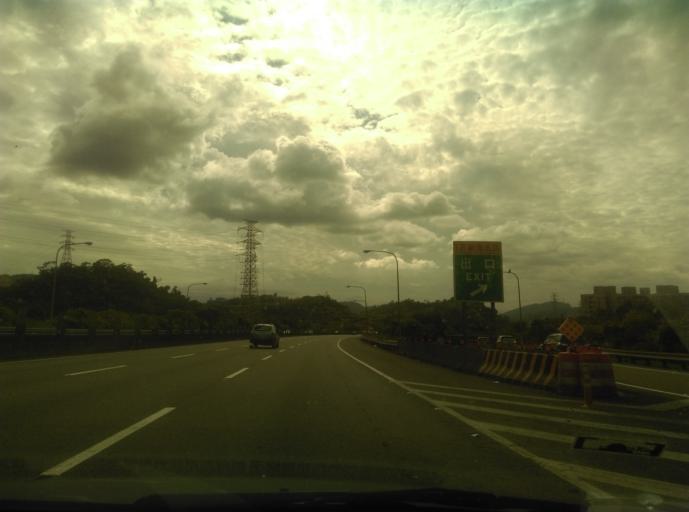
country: TW
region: Taipei
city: Taipei
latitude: 25.0586
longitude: 121.6405
